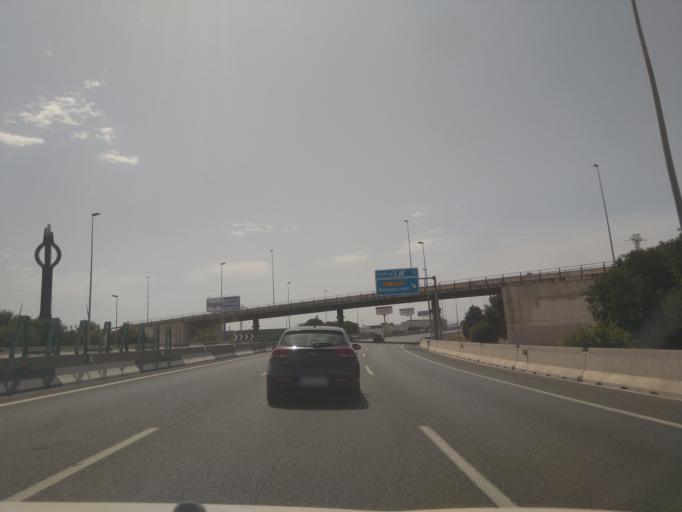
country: ES
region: Valencia
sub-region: Provincia de Valencia
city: Beniparrell
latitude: 39.3786
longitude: -0.4019
